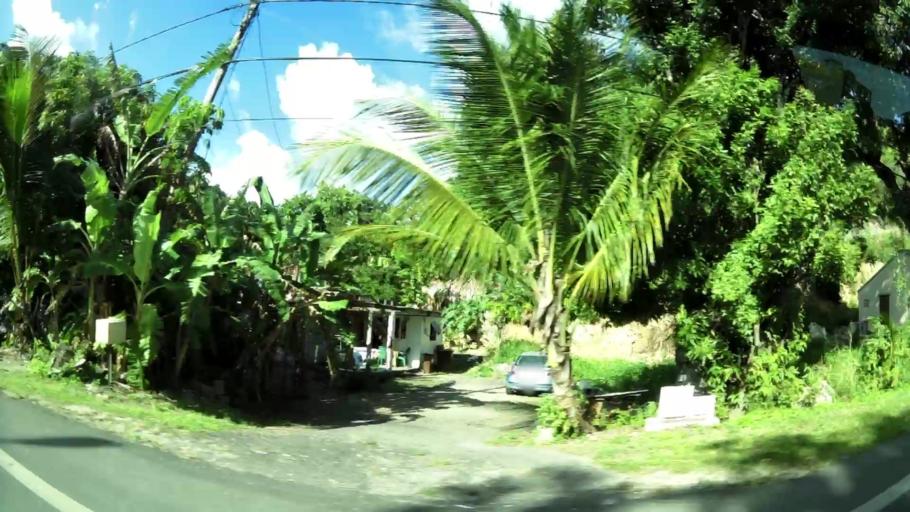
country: GP
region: Guadeloupe
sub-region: Guadeloupe
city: Le Gosier
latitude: 16.2180
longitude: -61.4978
